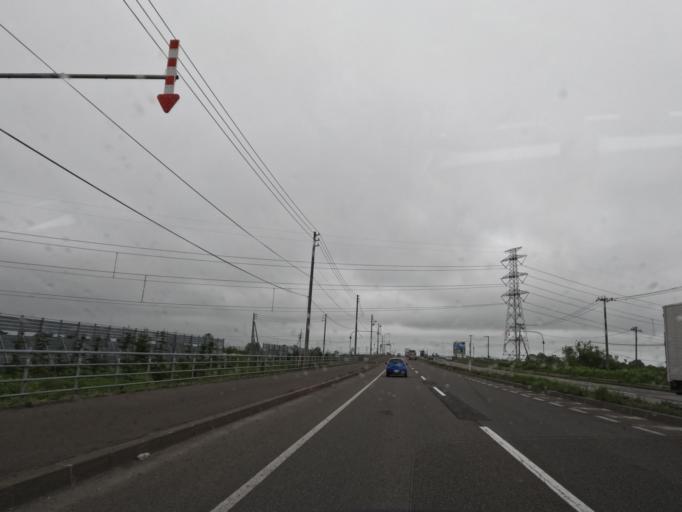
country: JP
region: Hokkaido
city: Tobetsu
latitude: 43.1607
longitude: 141.5194
